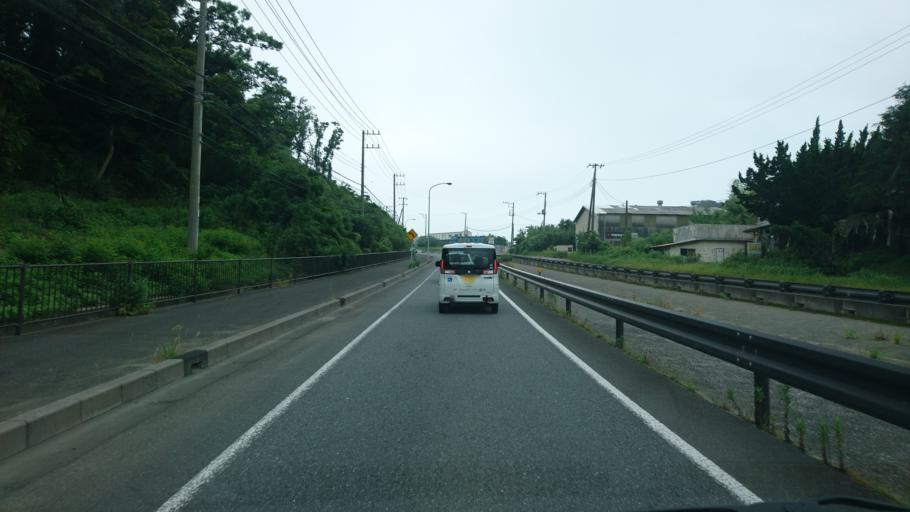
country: JP
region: Chiba
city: Kimitsu
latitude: 35.2470
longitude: 139.8874
